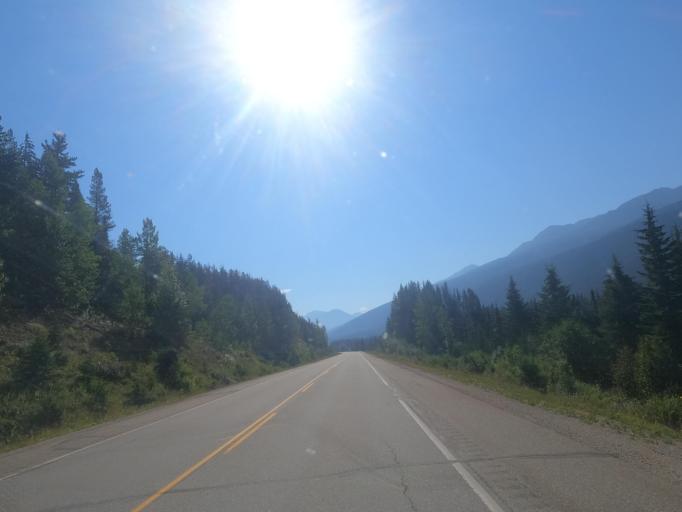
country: CA
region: Alberta
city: Jasper Park Lodge
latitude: 52.8900
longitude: -118.7272
